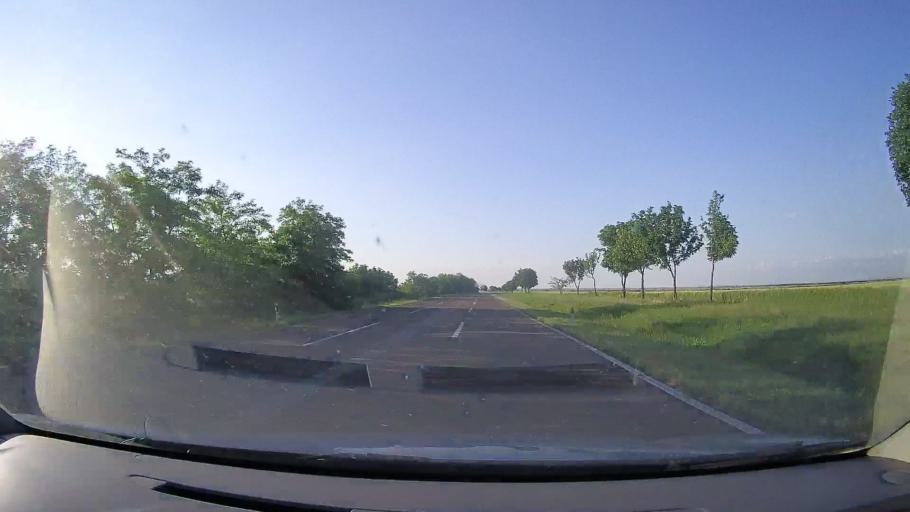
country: RO
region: Timis
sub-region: Comuna Moravita
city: Moravita
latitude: 45.2132
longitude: 21.2997
